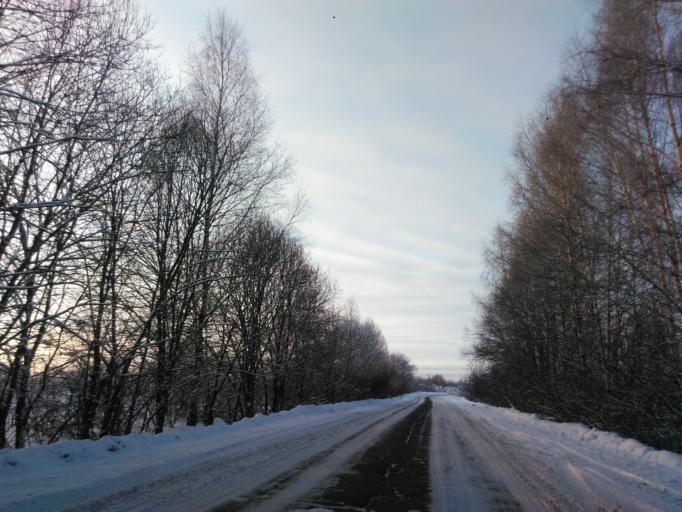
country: RU
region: Tverskaya
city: Zavidovo
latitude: 56.6329
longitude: 36.6205
